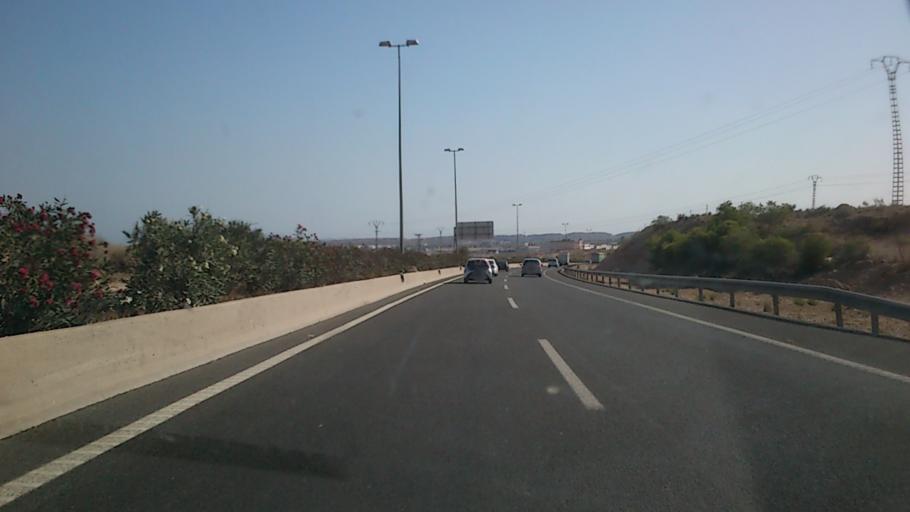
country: ES
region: Valencia
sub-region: Provincia de Alicante
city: San Vicent del Raspeig
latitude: 38.3589
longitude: -0.5363
